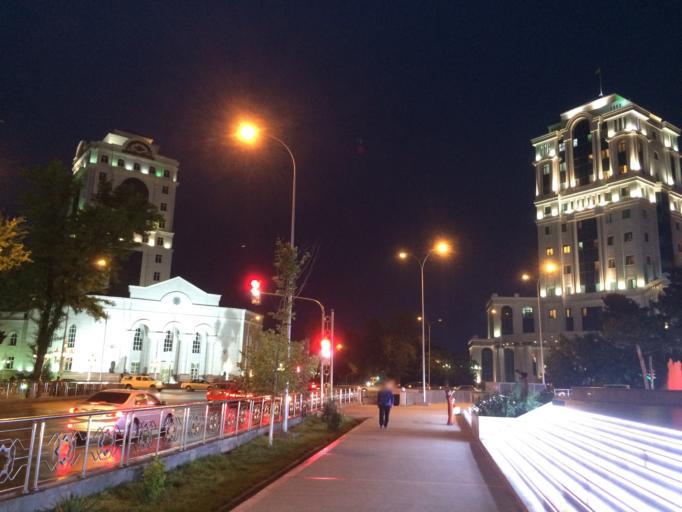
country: TM
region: Ahal
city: Ashgabat
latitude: 37.9399
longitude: 58.3920
